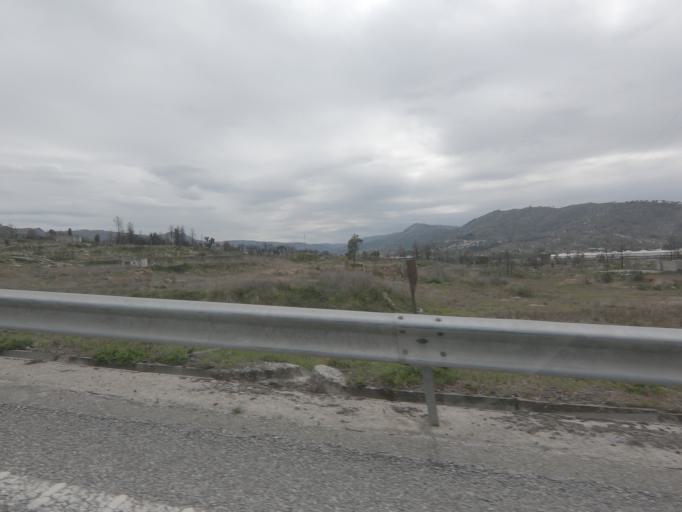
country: PT
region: Guarda
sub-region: Guarda
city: Guarda
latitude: 40.6208
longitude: -7.2898
